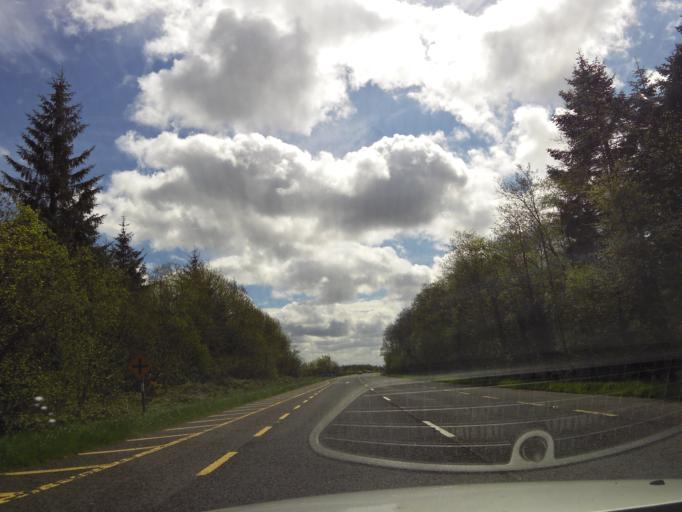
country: IE
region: Connaught
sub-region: Maigh Eo
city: Claremorris
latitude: 53.6982
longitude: -8.9771
